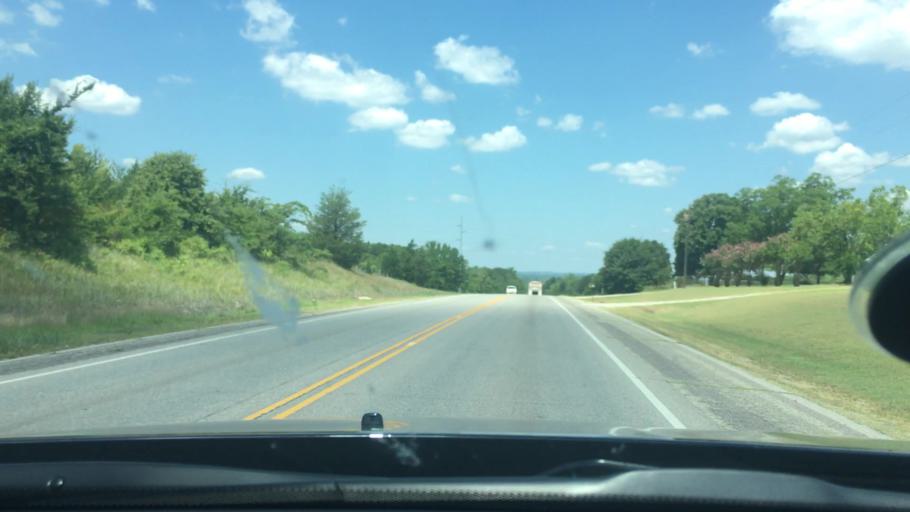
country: US
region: Oklahoma
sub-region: Marshall County
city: Oakland
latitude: 34.1547
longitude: -96.8175
